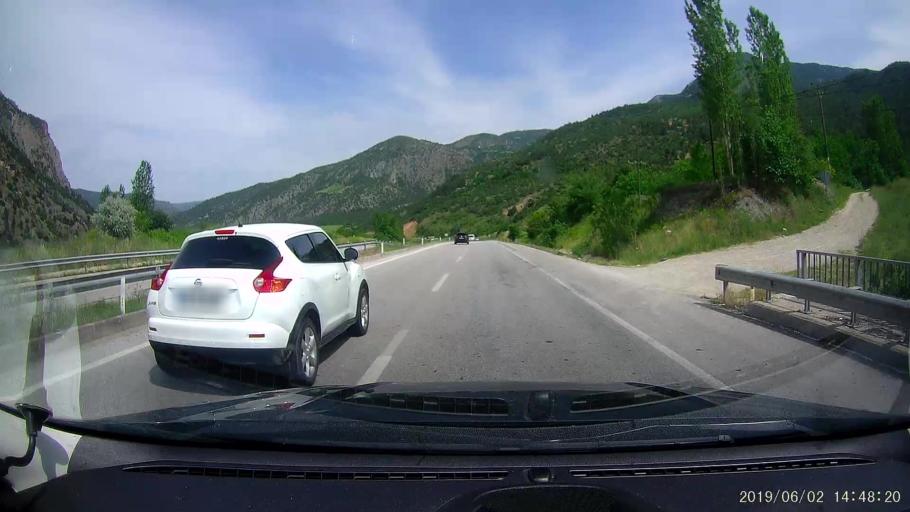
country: TR
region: Corum
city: Hacihamza
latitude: 41.0634
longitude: 34.4781
